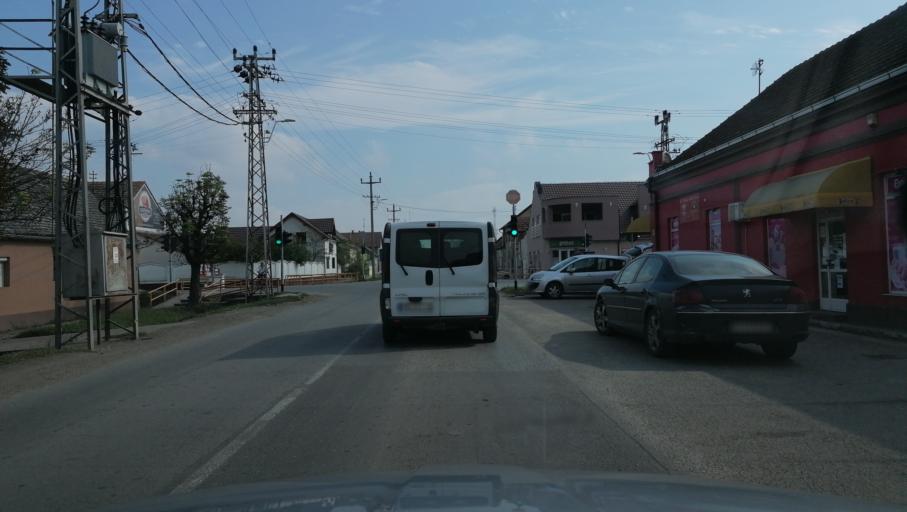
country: RS
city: Ravnje
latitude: 45.0232
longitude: 19.4029
